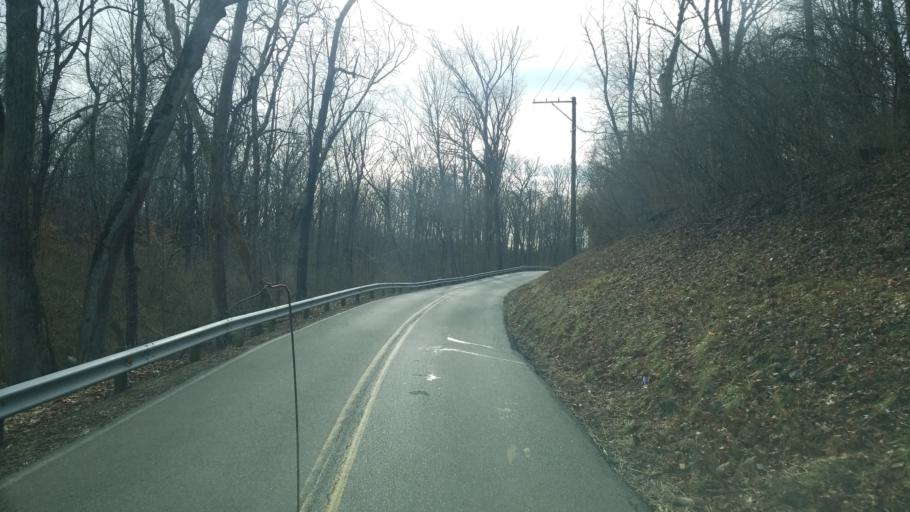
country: US
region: Ohio
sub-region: Warren County
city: Lebanon
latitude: 39.4255
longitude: -84.1598
